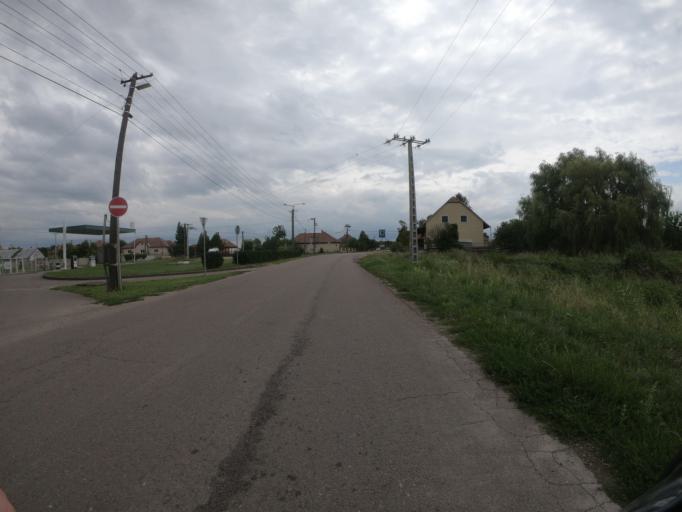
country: HU
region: Borsod-Abauj-Zemplen
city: Szentistvan
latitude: 47.7703
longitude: 20.6658
